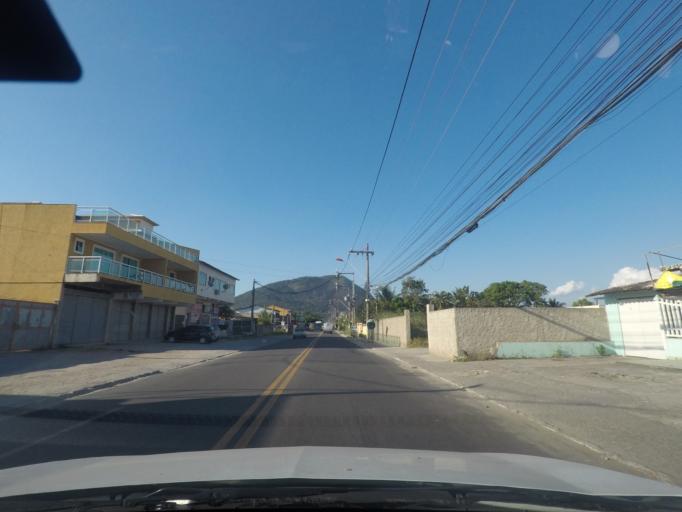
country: BR
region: Rio de Janeiro
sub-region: Marica
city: Marica
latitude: -22.9610
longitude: -42.9621
